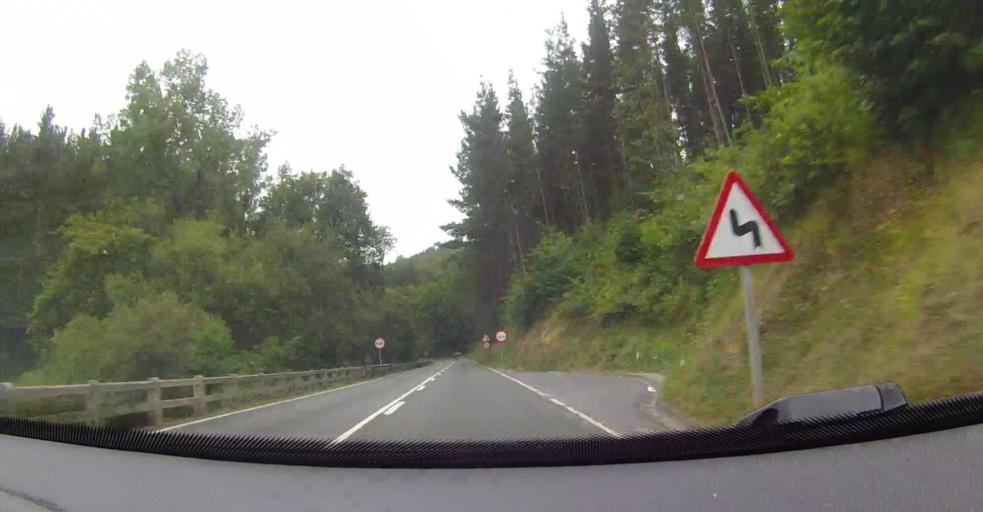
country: ES
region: Basque Country
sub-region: Bizkaia
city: Balmaseda
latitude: 43.2411
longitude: -3.2292
